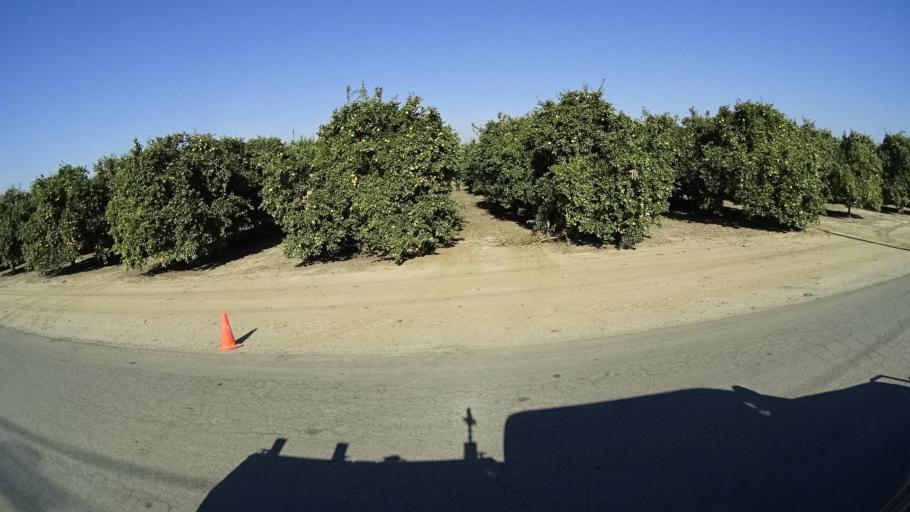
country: US
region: California
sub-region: Tulare County
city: Richgrove
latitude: 35.7180
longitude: -119.1390
